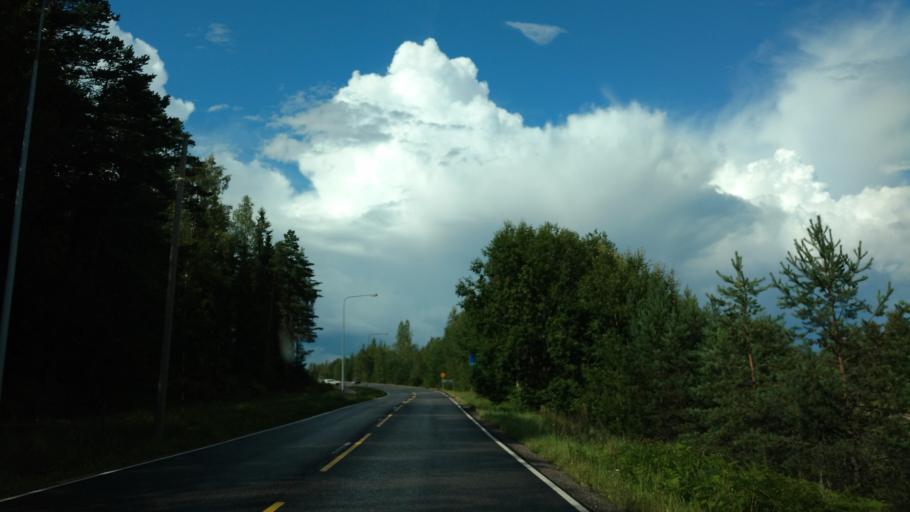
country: FI
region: Varsinais-Suomi
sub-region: Turku
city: Paimio
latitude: 60.4241
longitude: 22.7272
